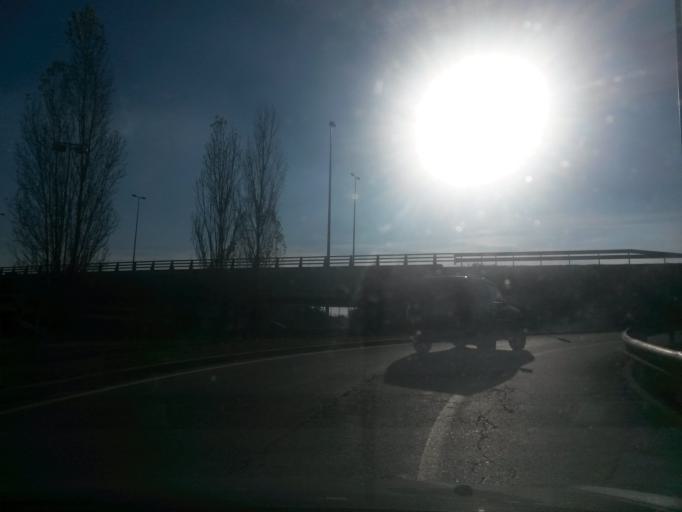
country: ES
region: Catalonia
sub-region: Provincia de Girona
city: Salt
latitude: 41.9572
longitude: 2.8098
